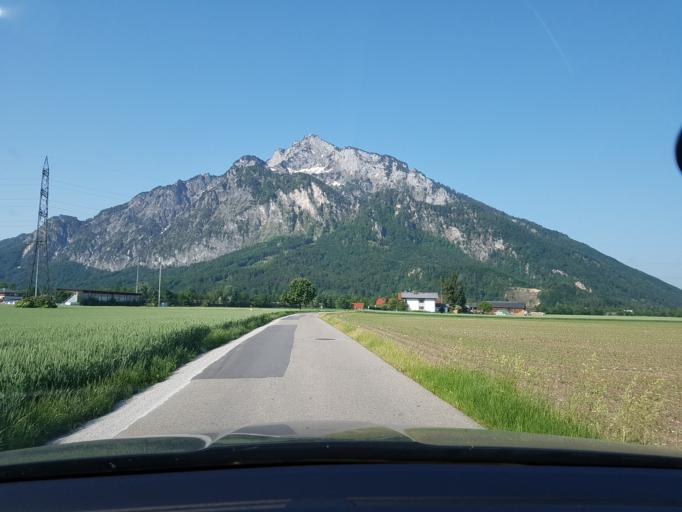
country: AT
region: Salzburg
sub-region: Politischer Bezirk Salzburg-Umgebung
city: Anif
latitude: 47.7462
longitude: 13.0491
